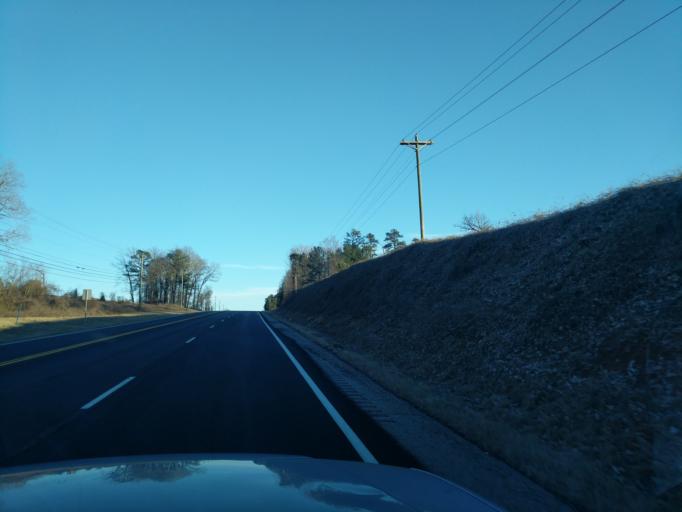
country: US
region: Georgia
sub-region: Stephens County
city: Toccoa
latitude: 34.5180
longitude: -83.2351
